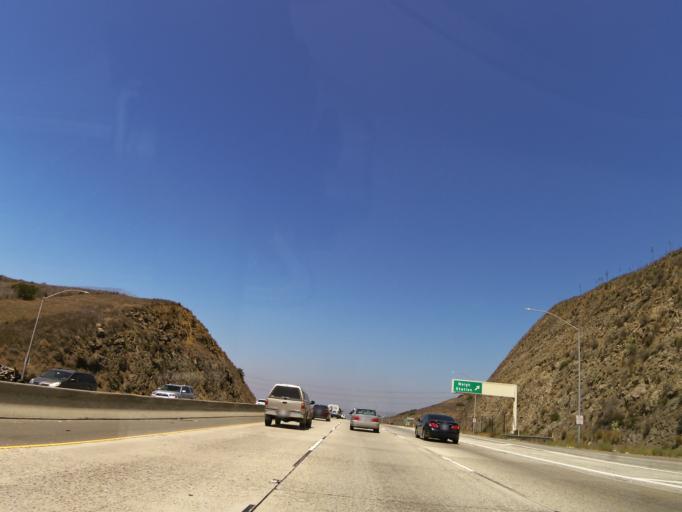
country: US
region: California
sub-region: Ventura County
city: Casa Conejo
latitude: 34.1982
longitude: -118.9541
